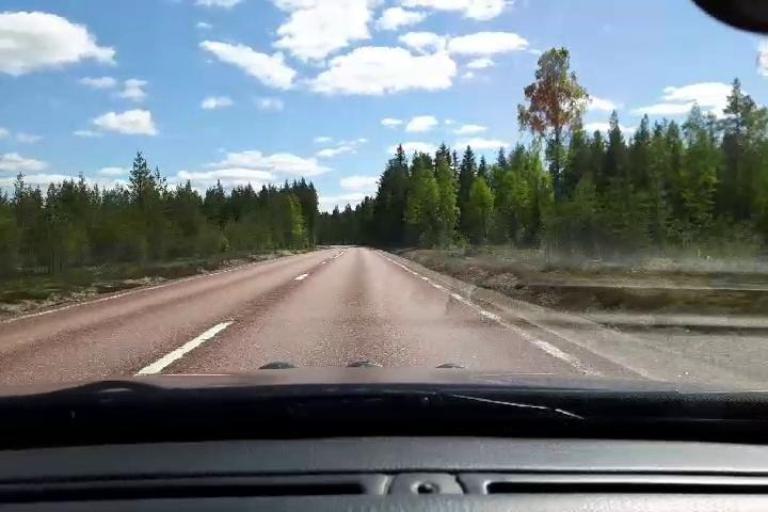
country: SE
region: Gaevleborg
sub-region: Ljusdals Kommun
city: Farila
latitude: 61.9092
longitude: 15.6294
